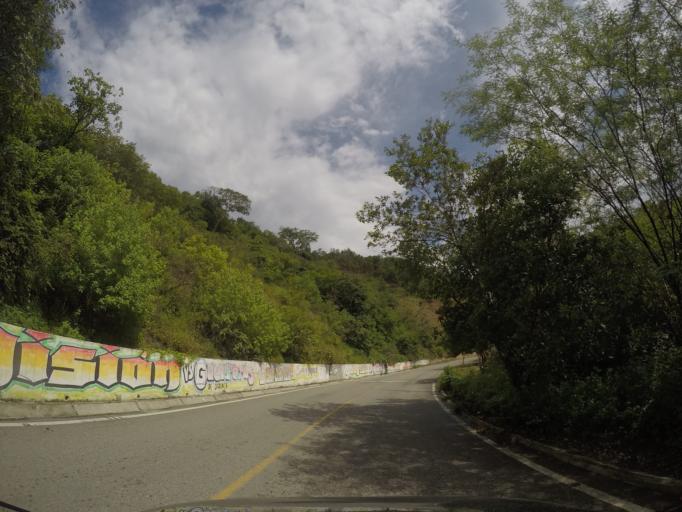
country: MX
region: Oaxaca
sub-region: San Jeronimo Coatlan
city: San Cristobal Honduras
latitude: 16.3762
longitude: -97.0784
